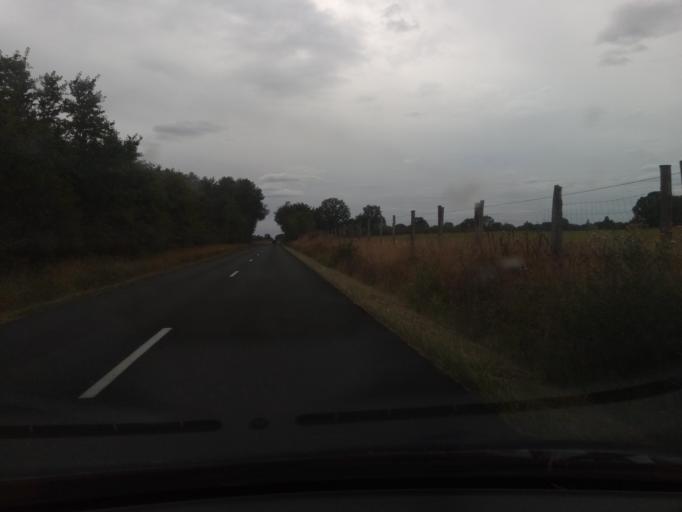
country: FR
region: Poitou-Charentes
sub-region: Departement de la Vienne
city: Pleumartin
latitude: 46.6651
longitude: 0.8023
